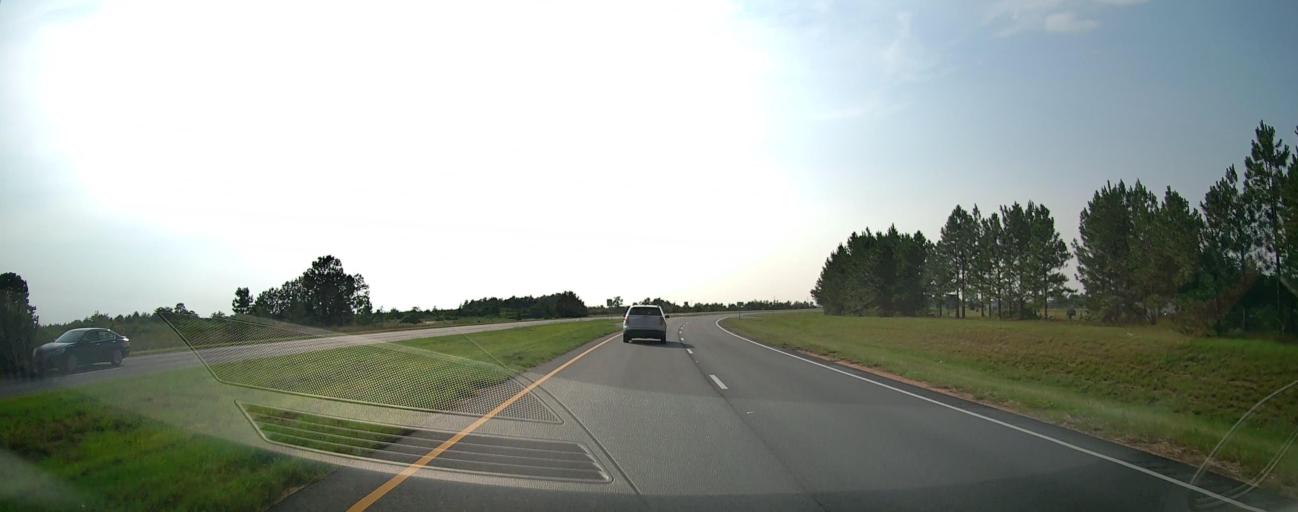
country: US
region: Georgia
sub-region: Taylor County
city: Butler
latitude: 32.5497
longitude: -84.2593
